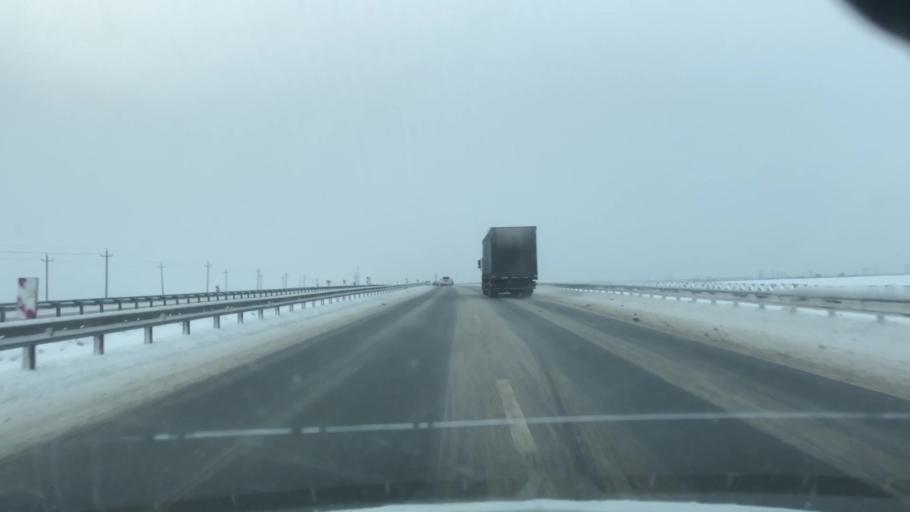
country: RU
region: Moskovskaya
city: Mikhnevo
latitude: 55.1079
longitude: 37.9261
